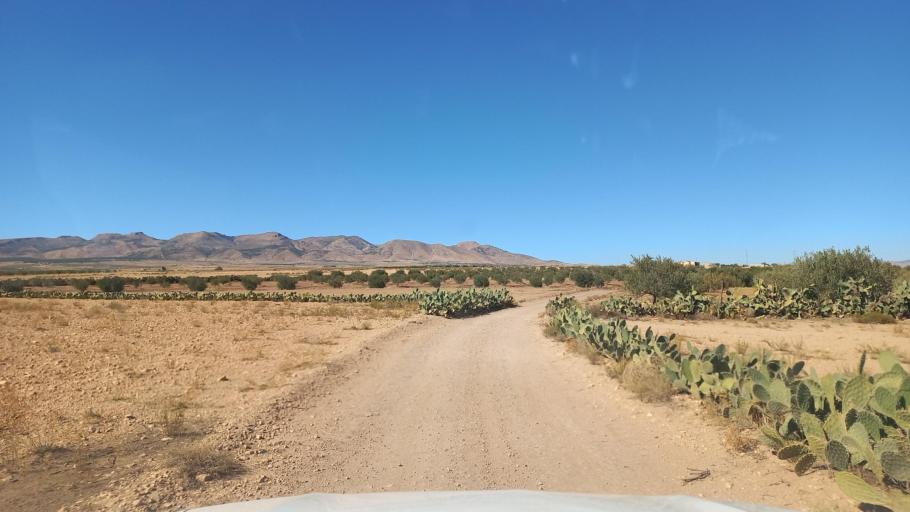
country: TN
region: Al Qasrayn
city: Sbiba
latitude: 35.3950
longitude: 9.0837
